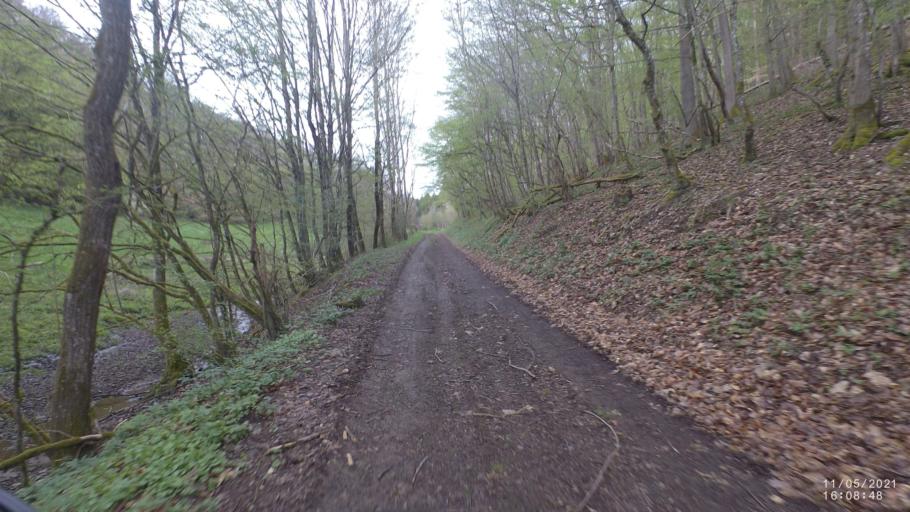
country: DE
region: Rheinland-Pfalz
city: Nachtsheim
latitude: 50.3098
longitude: 7.0657
